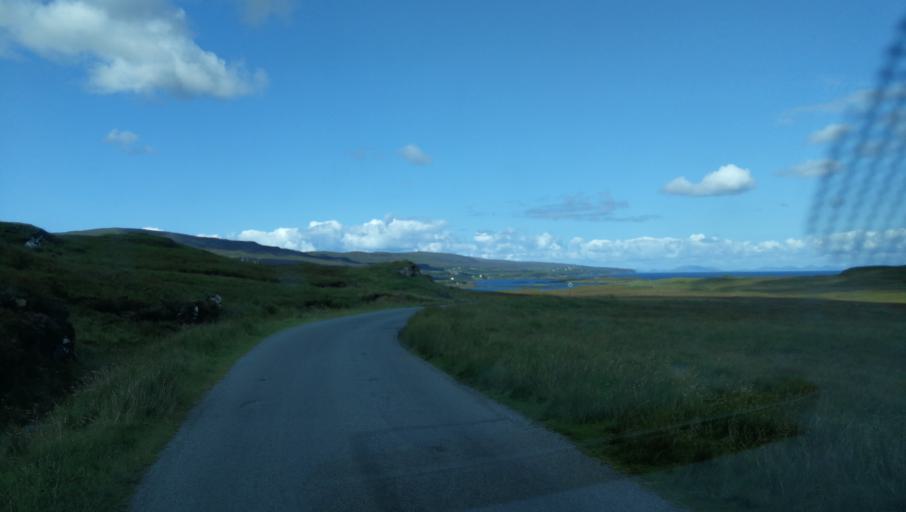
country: GB
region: Scotland
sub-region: Highland
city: Isle of Skye
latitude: 57.4280
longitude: -6.6064
